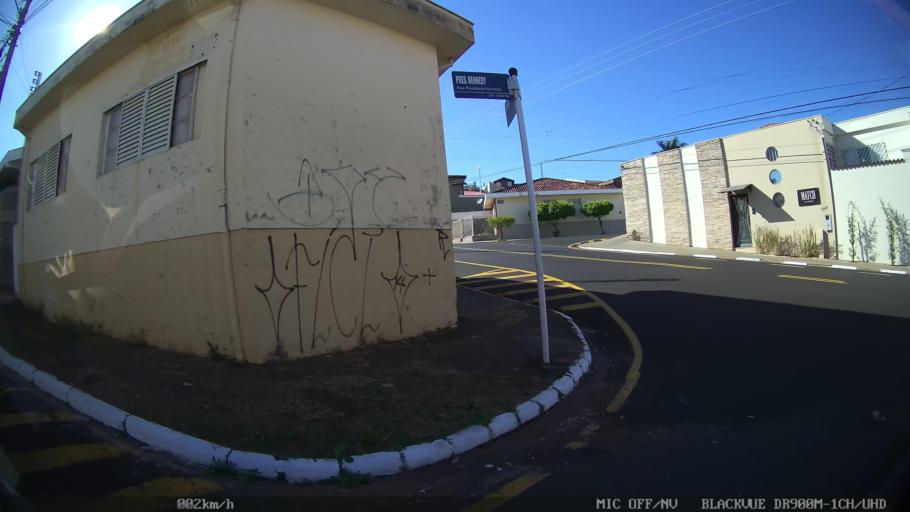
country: BR
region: Sao Paulo
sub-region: Franca
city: Franca
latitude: -20.5420
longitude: -47.4070
